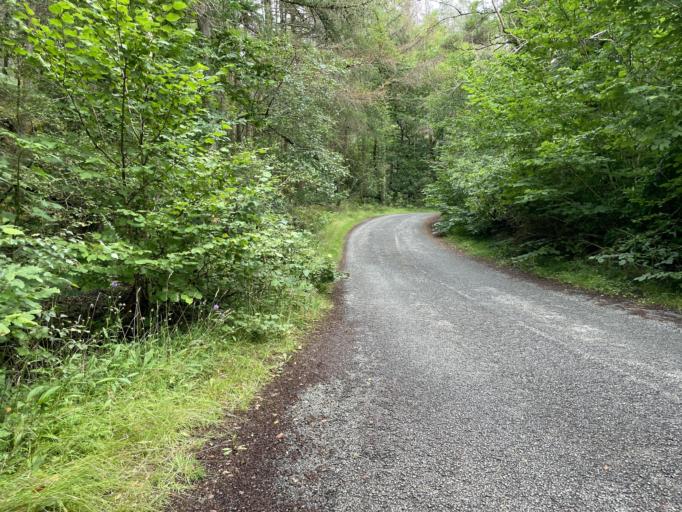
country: GB
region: Scotland
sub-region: Dumfries and Galloway
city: Newton Stewart
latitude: 55.0907
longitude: -4.4990
